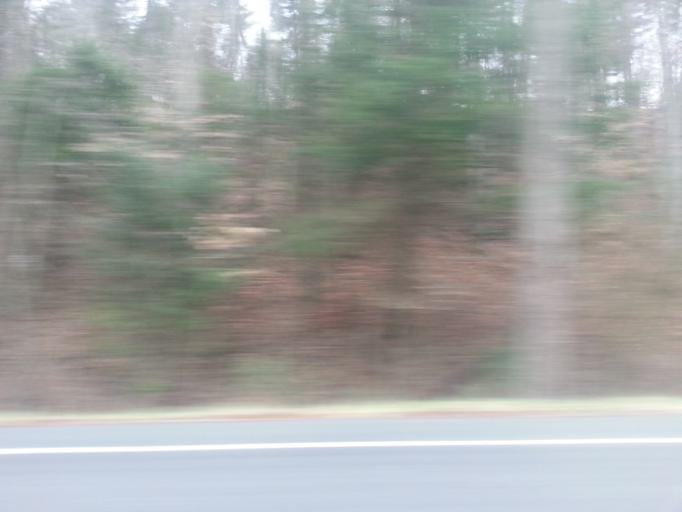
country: US
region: Tennessee
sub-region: Roane County
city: Harriman
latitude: 36.0255
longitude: -84.5248
